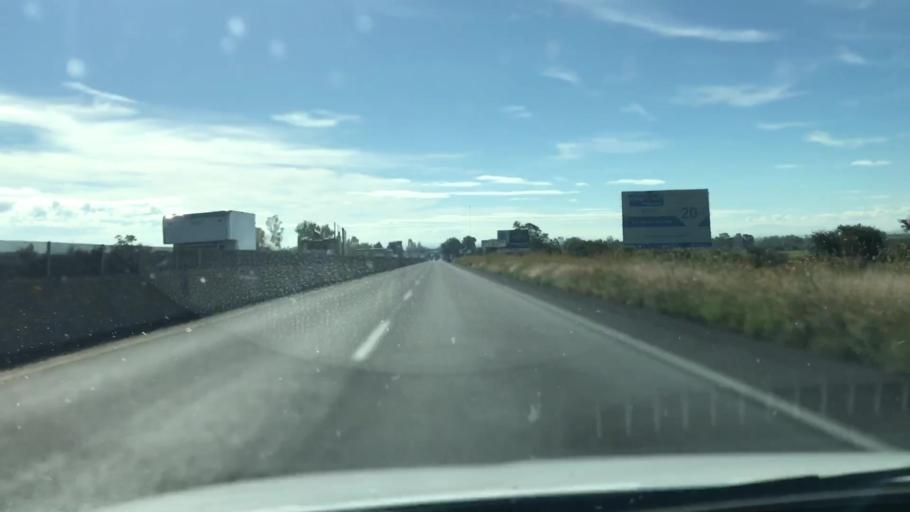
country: MX
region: Guanajuato
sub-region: Leon
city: Centro Familiar la Soledad
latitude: 21.1067
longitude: -101.7901
